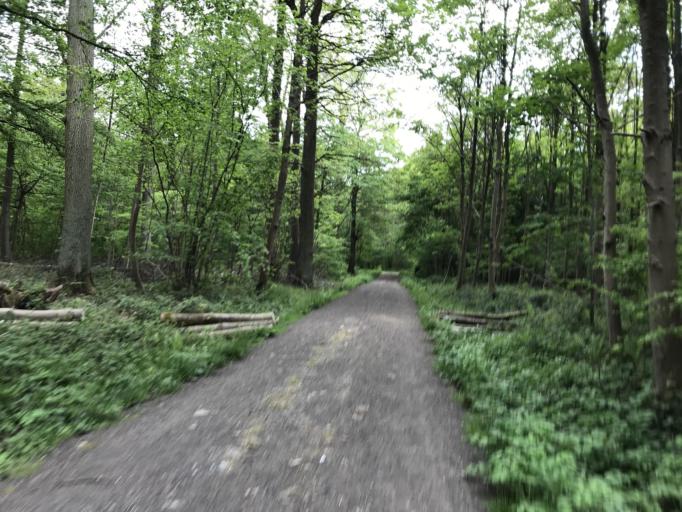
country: FR
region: Ile-de-France
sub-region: Departement de l'Essonne
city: Bievres
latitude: 48.7617
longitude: 2.2383
